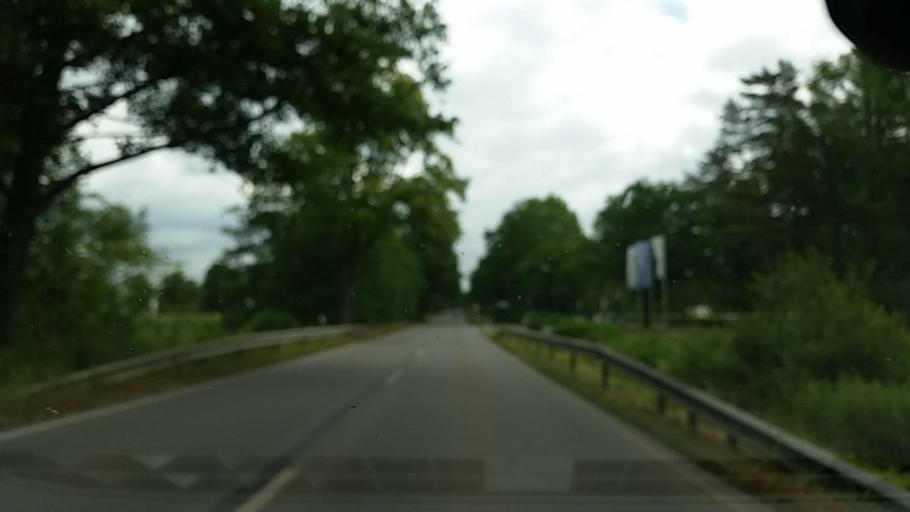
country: DE
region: Schleswig-Holstein
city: Kayhude
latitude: 53.7587
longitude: 10.1533
